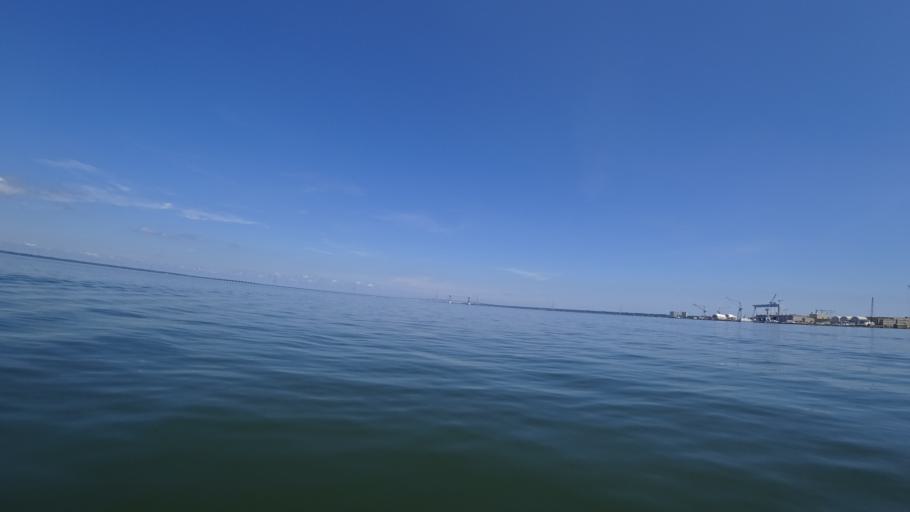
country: US
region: Virginia
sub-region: City of Newport News
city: Newport News
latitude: 36.9840
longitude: -76.4507
